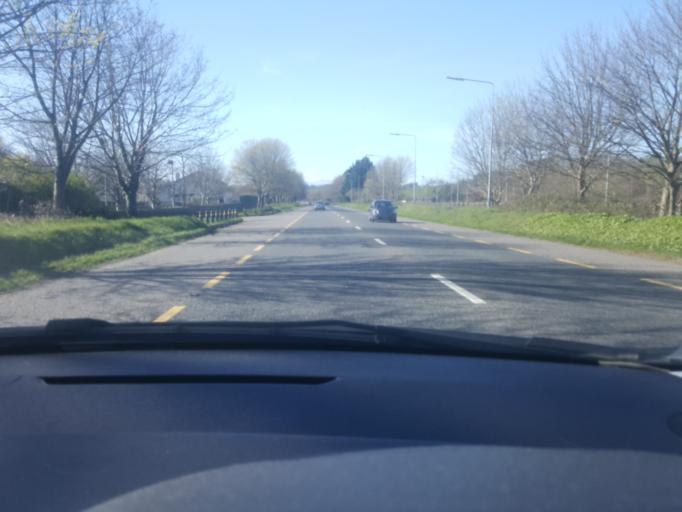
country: IE
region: Munster
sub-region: Ciarrai
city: Cill Airne
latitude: 52.0661
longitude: -9.4939
